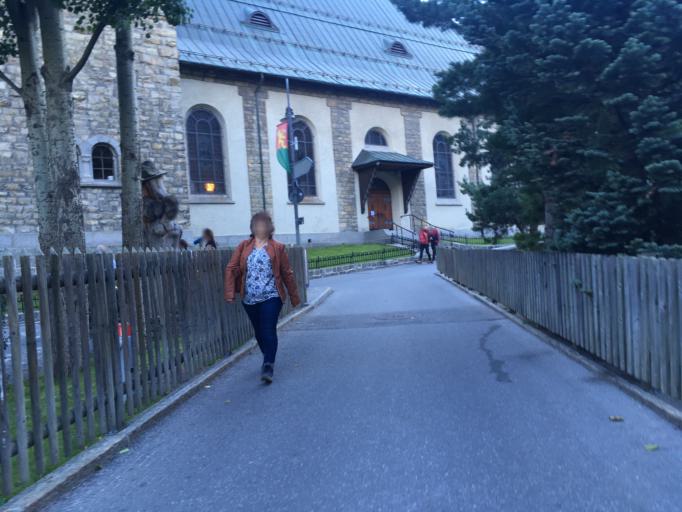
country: CH
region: Valais
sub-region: Visp District
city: Zermatt
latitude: 46.0198
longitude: 7.7469
